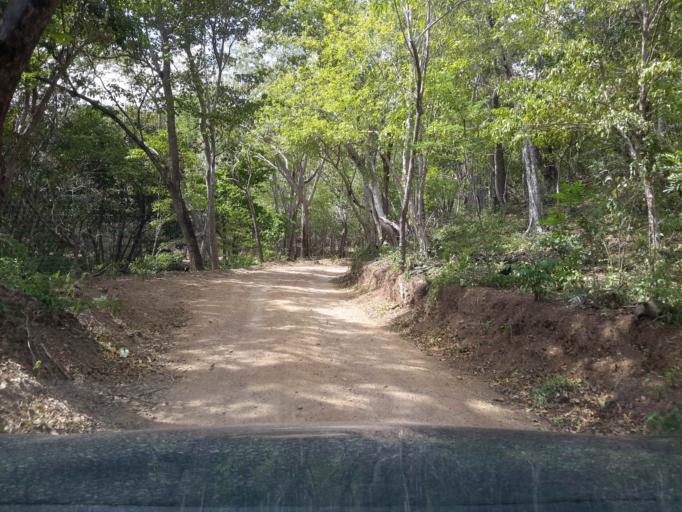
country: NI
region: Rivas
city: San Juan del Sur
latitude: 11.2203
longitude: -85.8302
